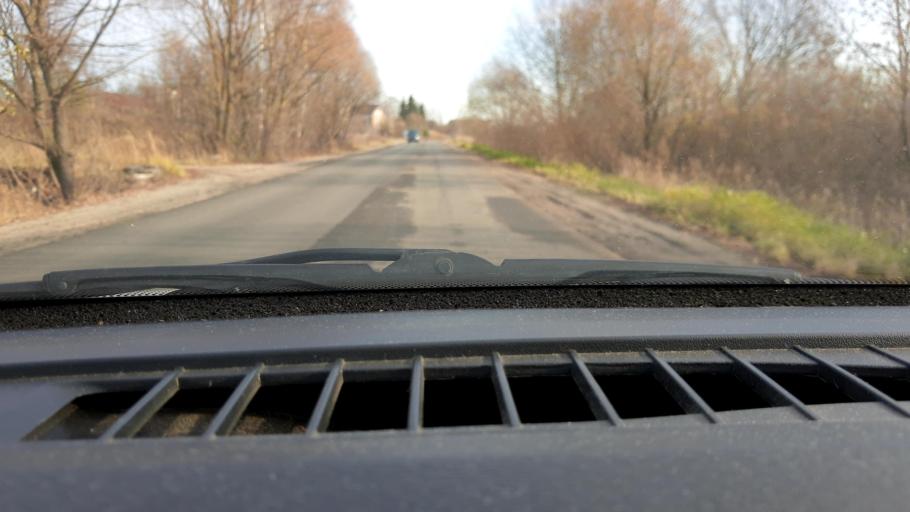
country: RU
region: Nizjnij Novgorod
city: Neklyudovo
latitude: 56.4211
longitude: 43.9571
